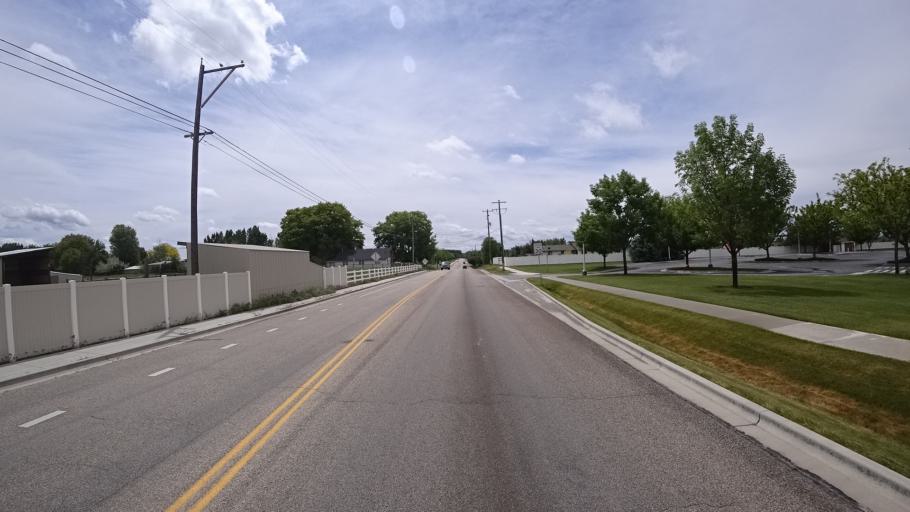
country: US
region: Idaho
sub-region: Ada County
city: Eagle
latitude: 43.7057
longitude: -116.4037
